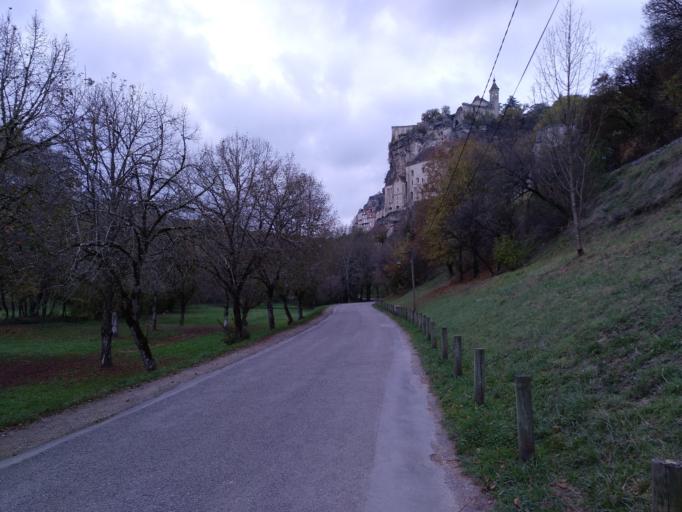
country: FR
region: Midi-Pyrenees
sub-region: Departement du Lot
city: Gramat
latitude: 44.8015
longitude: 1.6209
